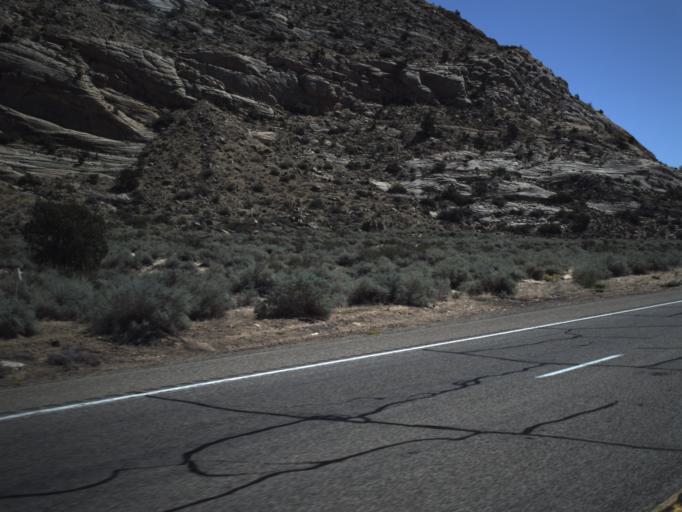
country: US
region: Utah
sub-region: Washington County
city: Ivins
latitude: 37.2336
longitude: -113.6346
